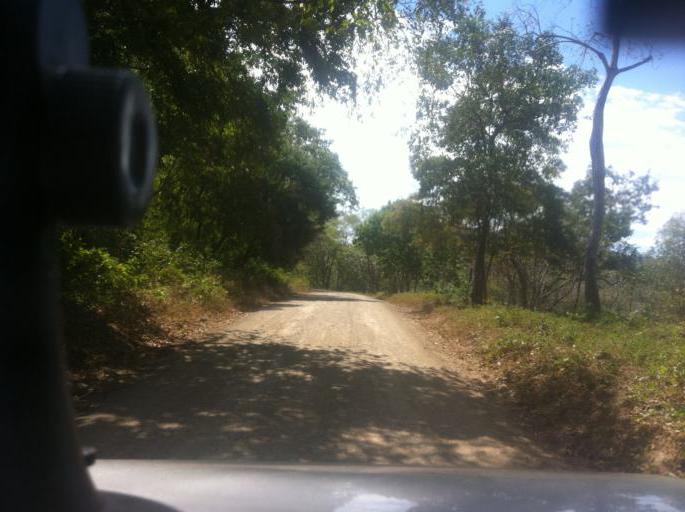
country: NI
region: Rivas
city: Belen
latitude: 11.5643
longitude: -86.0294
